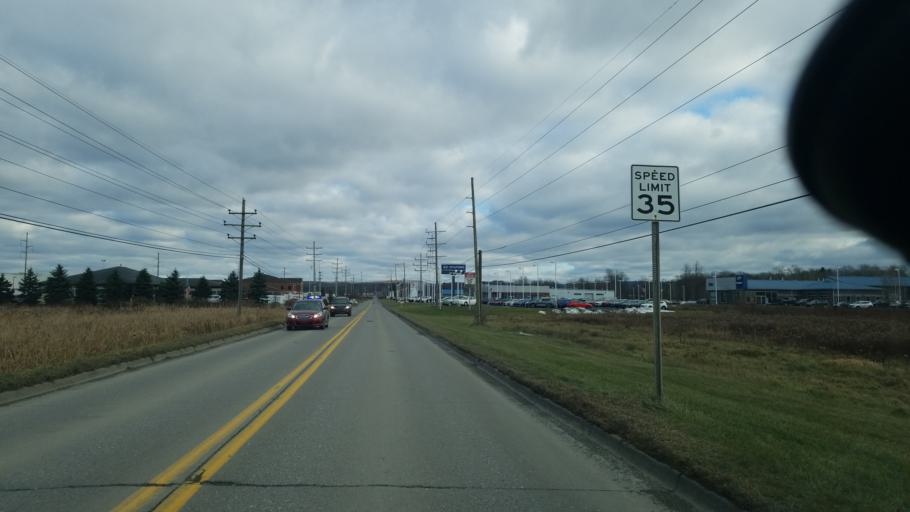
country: US
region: Pennsylvania
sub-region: Clearfield County
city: DuBois
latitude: 41.1212
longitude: -78.7416
